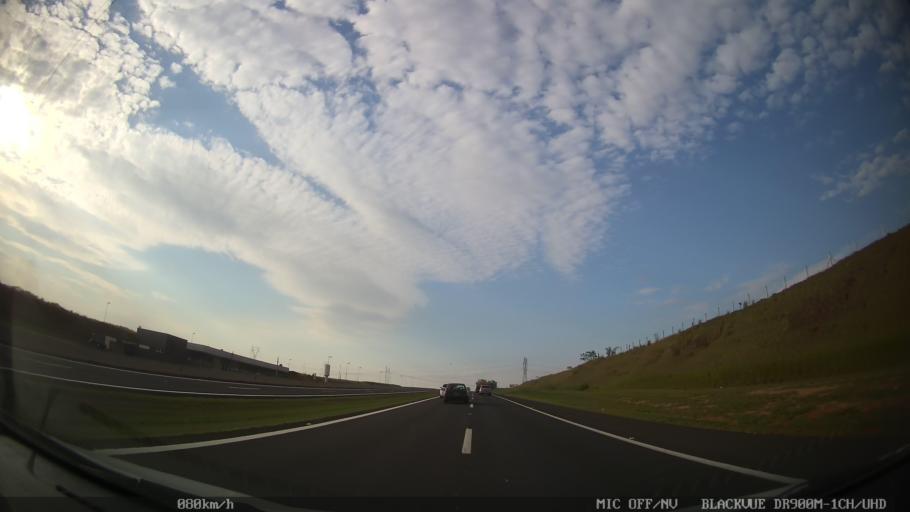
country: BR
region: Sao Paulo
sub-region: Artur Nogueira
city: Artur Nogueira
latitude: -22.6065
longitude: -47.1923
